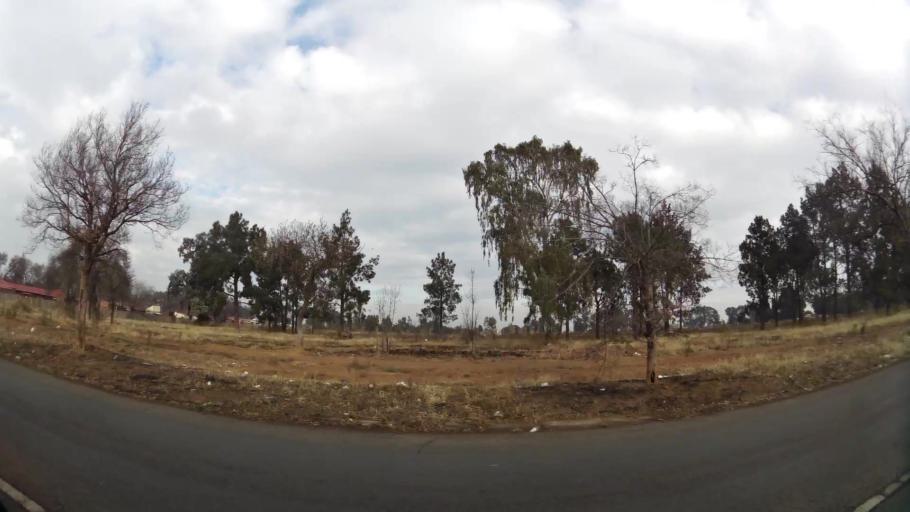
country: ZA
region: Gauteng
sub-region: Sedibeng District Municipality
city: Vanderbijlpark
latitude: -26.6977
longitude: 27.8125
